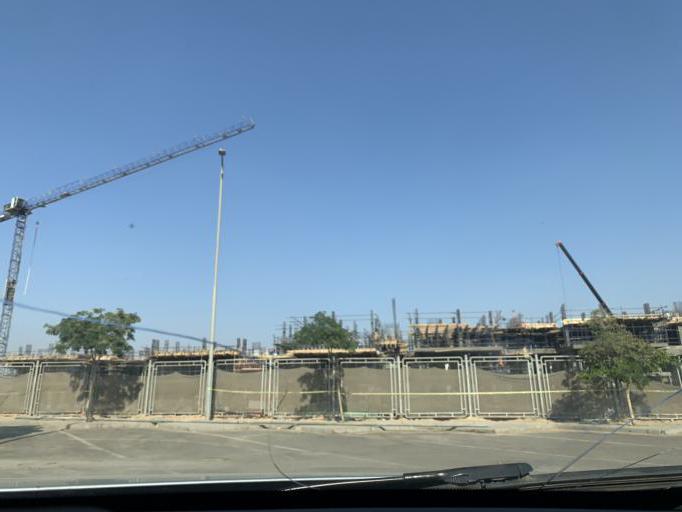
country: EG
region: Muhafazat al Qahirah
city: Cairo
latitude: 30.0322
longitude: 31.4057
